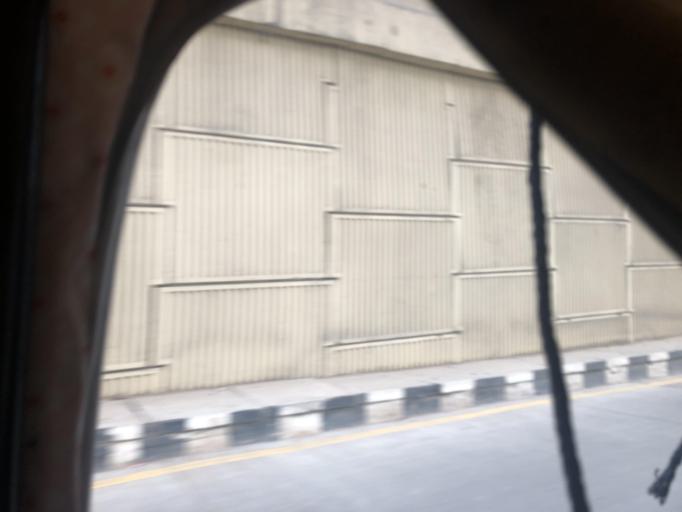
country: IN
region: Haryana
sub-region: Gurgaon
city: Gurgaon
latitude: 28.4705
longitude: 77.0571
